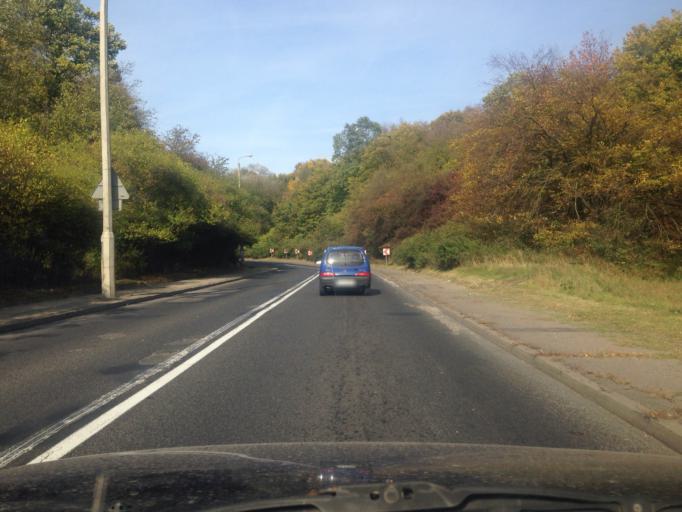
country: PL
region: Kujawsko-Pomorskie
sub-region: Powiat wloclawski
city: Fabianki
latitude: 52.6657
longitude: 19.1364
